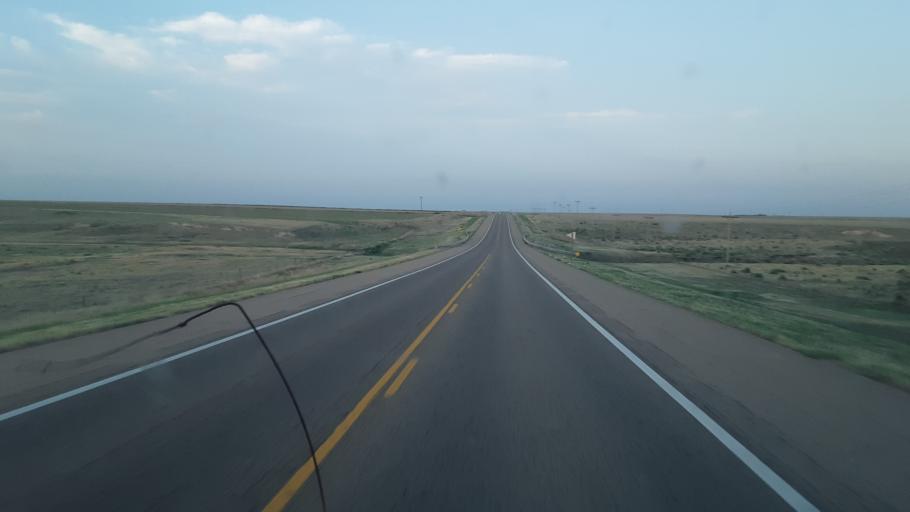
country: US
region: Kansas
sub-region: Kearny County
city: Lakin
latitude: 37.9440
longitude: -101.4463
